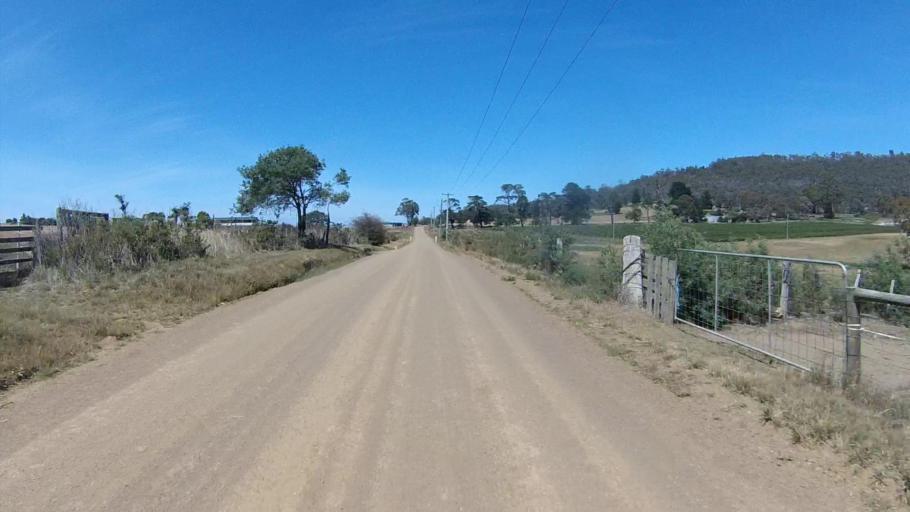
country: AU
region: Tasmania
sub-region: Sorell
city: Sorell
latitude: -42.7848
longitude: 147.6388
